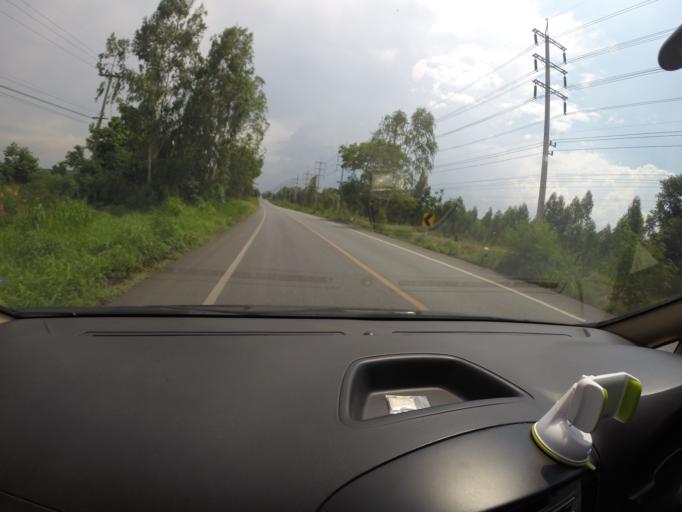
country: TH
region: Nakhon Ratchasima
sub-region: Amphoe Thepharak
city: Thepharak
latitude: 15.1154
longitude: 101.4669
